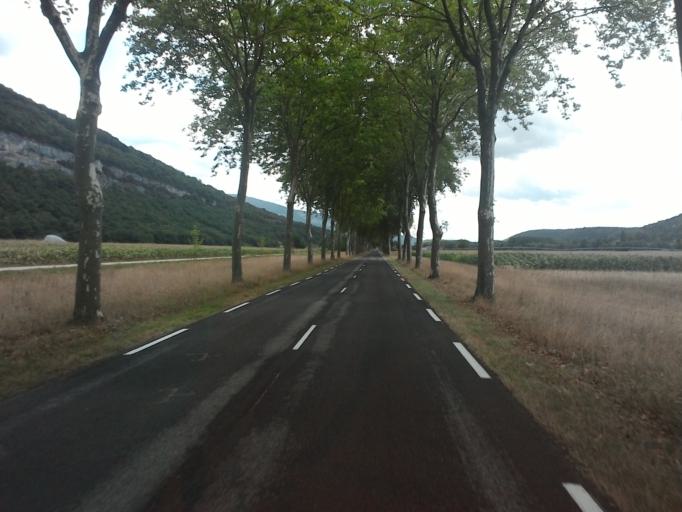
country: FR
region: Rhone-Alpes
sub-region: Departement de l'Ain
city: Saint-Sorlin-en-Bugey
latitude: 45.8744
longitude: 5.3833
